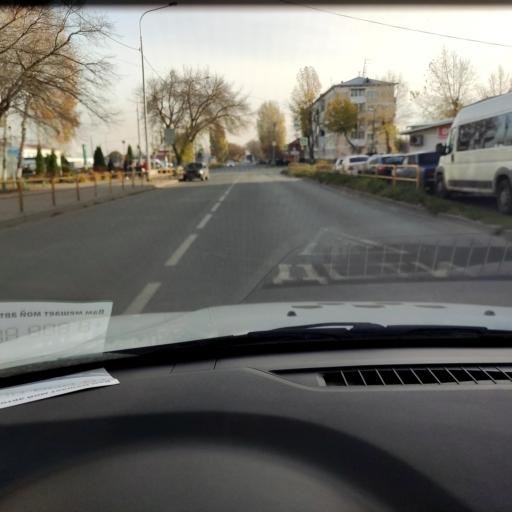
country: RU
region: Samara
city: Tol'yatti
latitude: 53.5374
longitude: 49.4085
